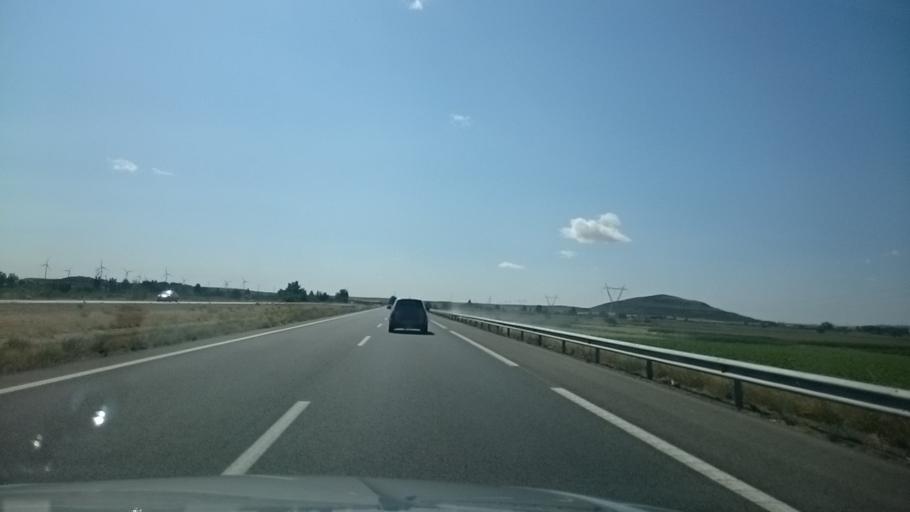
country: ES
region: Aragon
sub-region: Provincia de Zaragoza
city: Frescano
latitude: 41.9005
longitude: -1.4433
